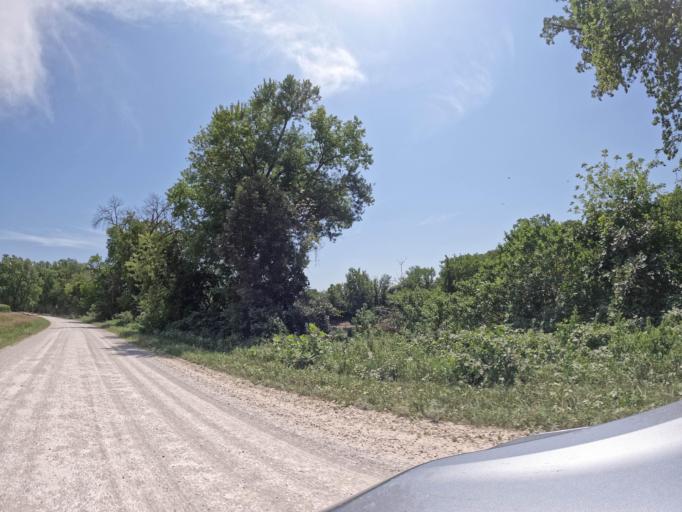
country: US
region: Iowa
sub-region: Henry County
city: Mount Pleasant
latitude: 40.9328
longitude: -91.6046
